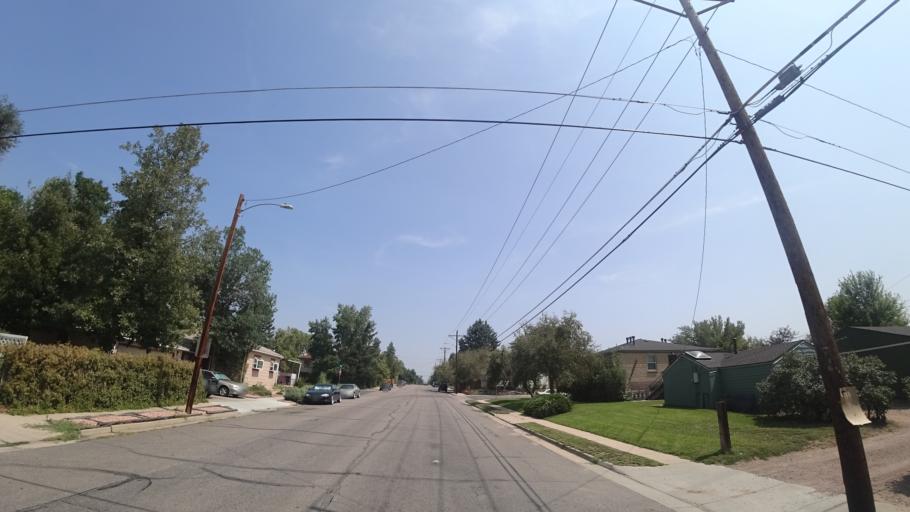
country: US
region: Colorado
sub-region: Arapahoe County
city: Englewood
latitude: 39.6386
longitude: -104.9933
